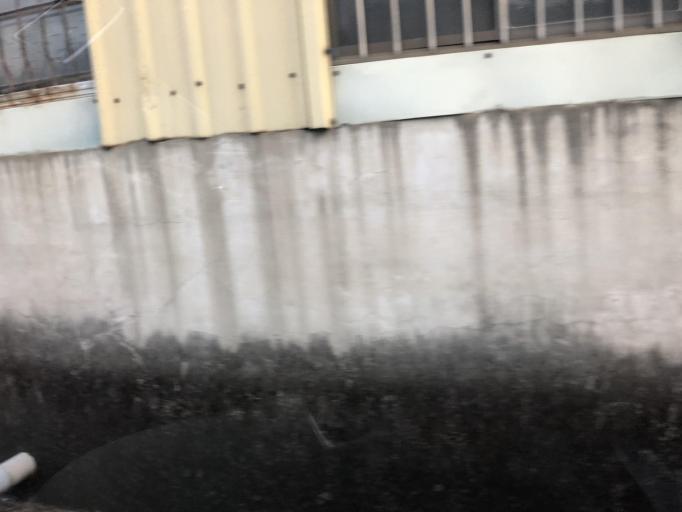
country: TW
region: Taiwan
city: Xinying
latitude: 23.1480
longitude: 120.2723
